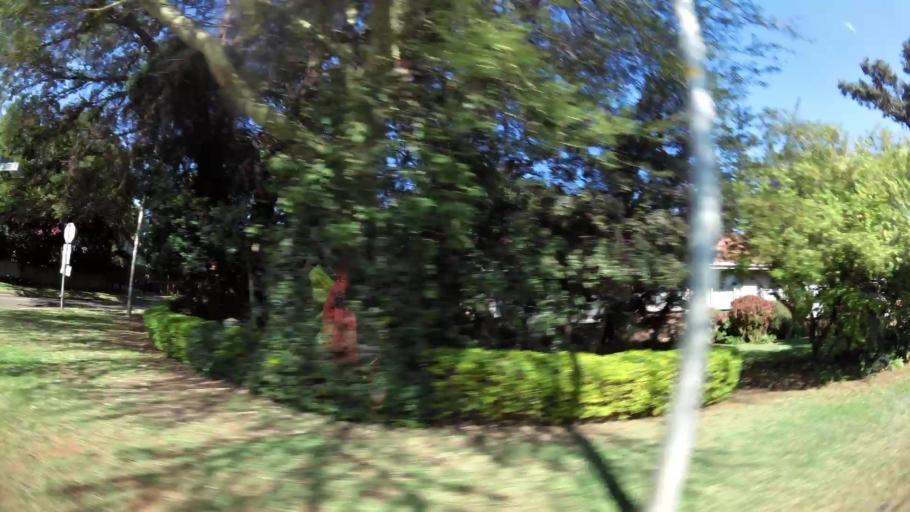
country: ZA
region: Gauteng
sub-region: City of Tshwane Metropolitan Municipality
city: Pretoria
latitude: -25.6850
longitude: 28.2304
